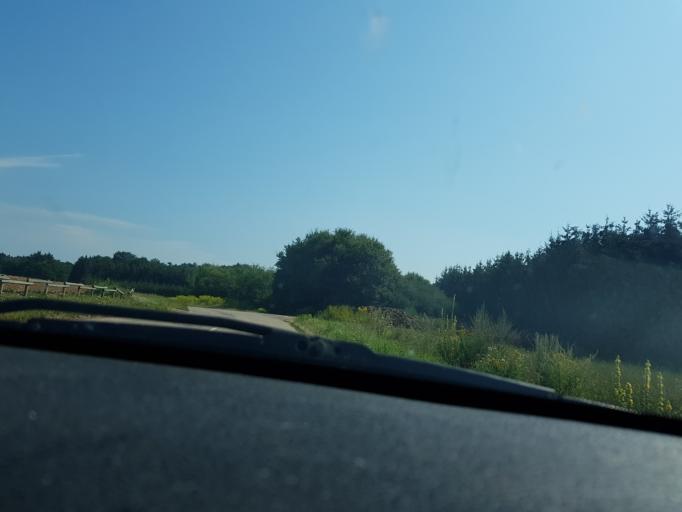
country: FR
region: Lorraine
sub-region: Departement de la Moselle
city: Longeville-les-Saint-Avold
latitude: 49.1224
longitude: 6.6522
